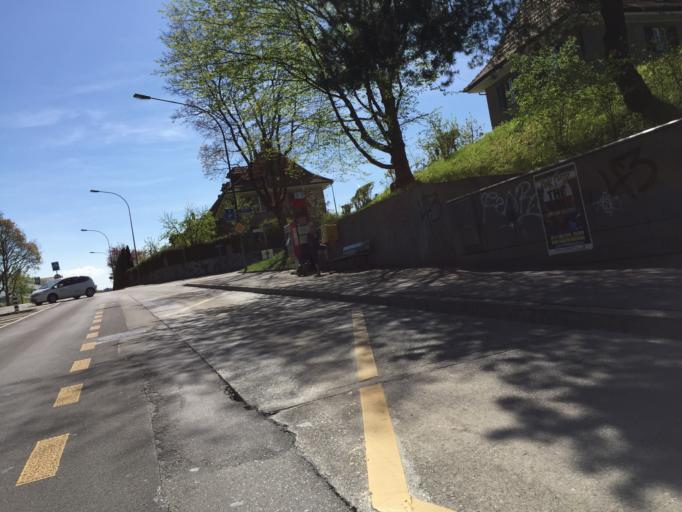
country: CH
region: Bern
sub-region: Bern-Mittelland District
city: Koniz
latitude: 46.9367
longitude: 7.4255
